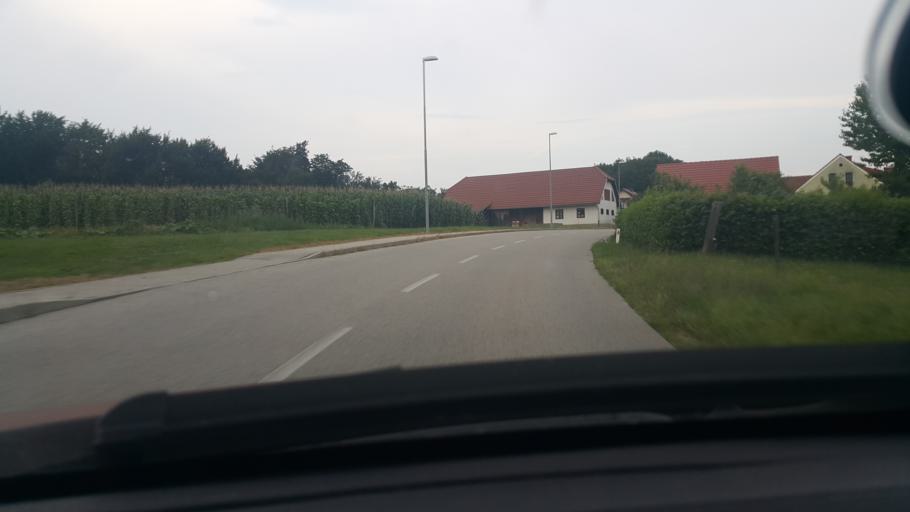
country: SI
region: Brezice
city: Brezice
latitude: 45.9243
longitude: 15.6684
